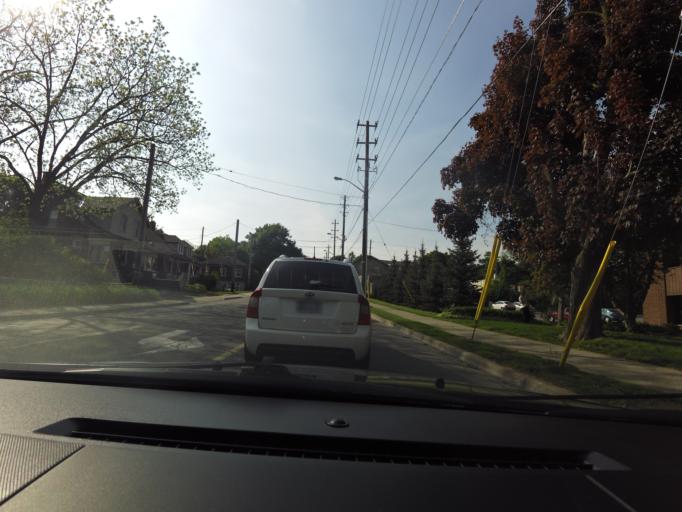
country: CA
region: Ontario
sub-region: Wellington County
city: Guelph
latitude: 43.5351
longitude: -80.2546
